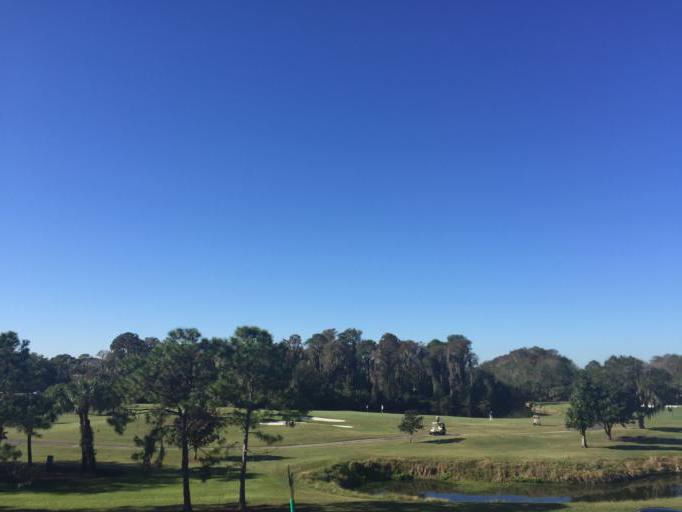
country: US
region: Florida
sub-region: Polk County
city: Citrus Ridge
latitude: 28.4059
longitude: -81.5873
